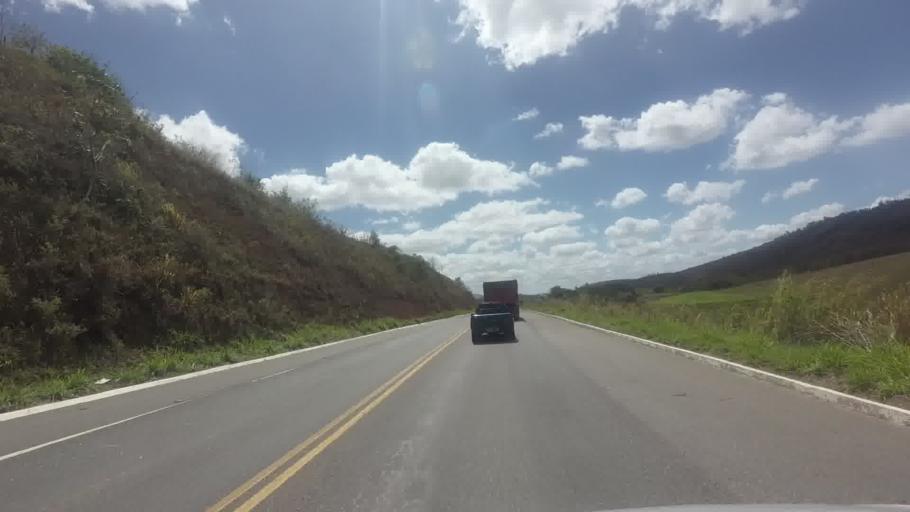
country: BR
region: Minas Gerais
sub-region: Recreio
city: Recreio
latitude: -21.6684
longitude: -42.3885
